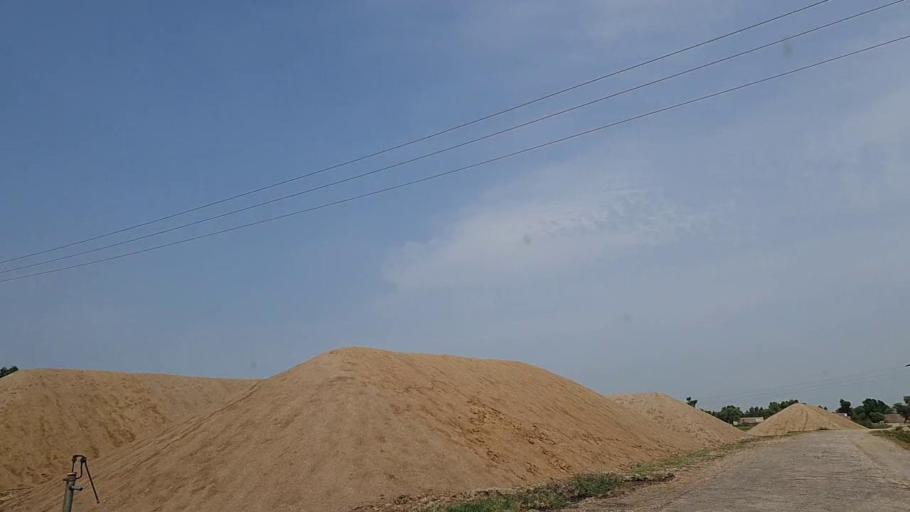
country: PK
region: Sindh
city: Khanpur
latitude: 27.8578
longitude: 69.4187
